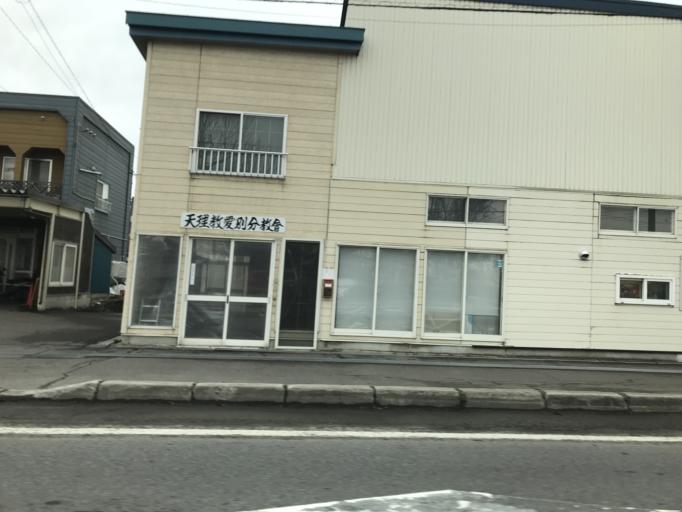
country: JP
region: Hokkaido
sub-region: Asahikawa-shi
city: Asahikawa
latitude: 43.8254
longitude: 142.4167
